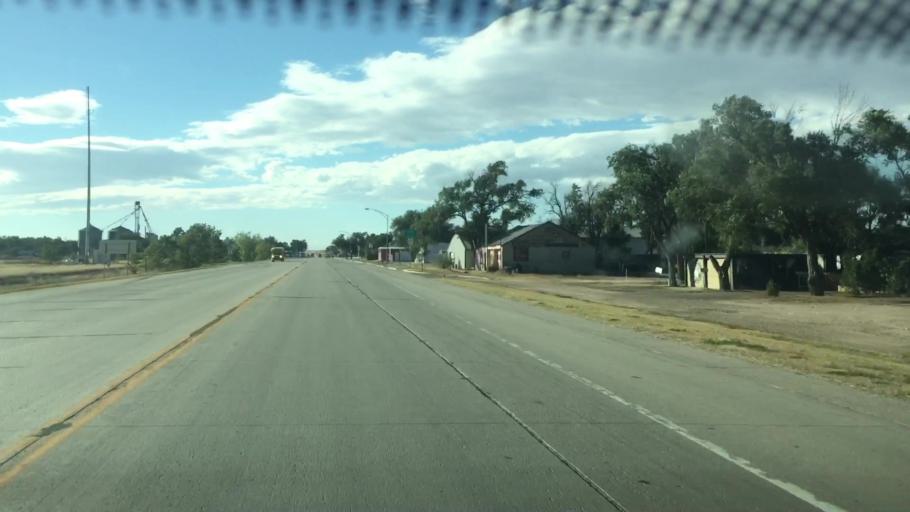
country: US
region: Colorado
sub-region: Lincoln County
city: Hugo
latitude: 39.1313
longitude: -103.4607
